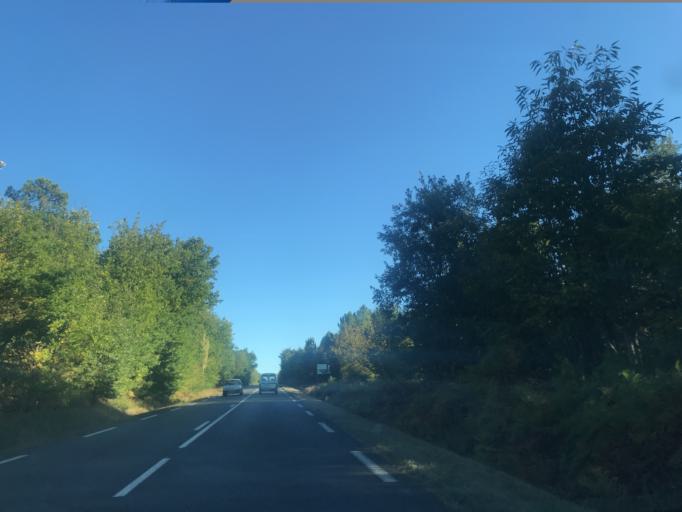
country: FR
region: Poitou-Charentes
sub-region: Departement de la Charente-Maritime
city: Montguyon
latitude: 45.1967
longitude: -0.1433
